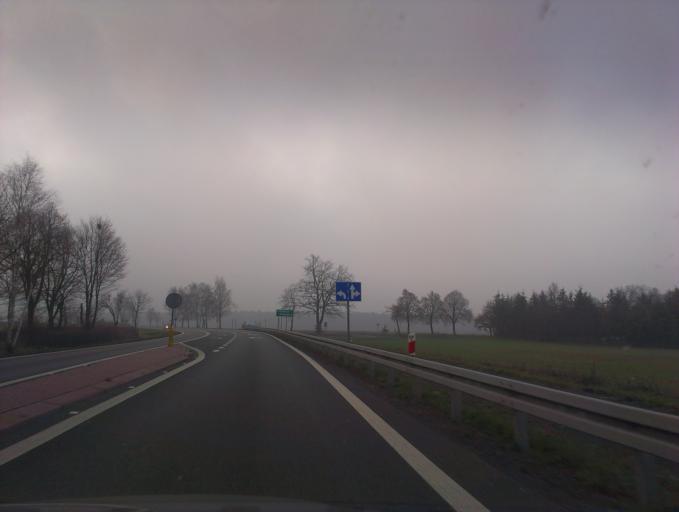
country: PL
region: Greater Poland Voivodeship
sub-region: Powiat chodzieski
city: Chodziez
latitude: 52.9527
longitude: 16.9401
